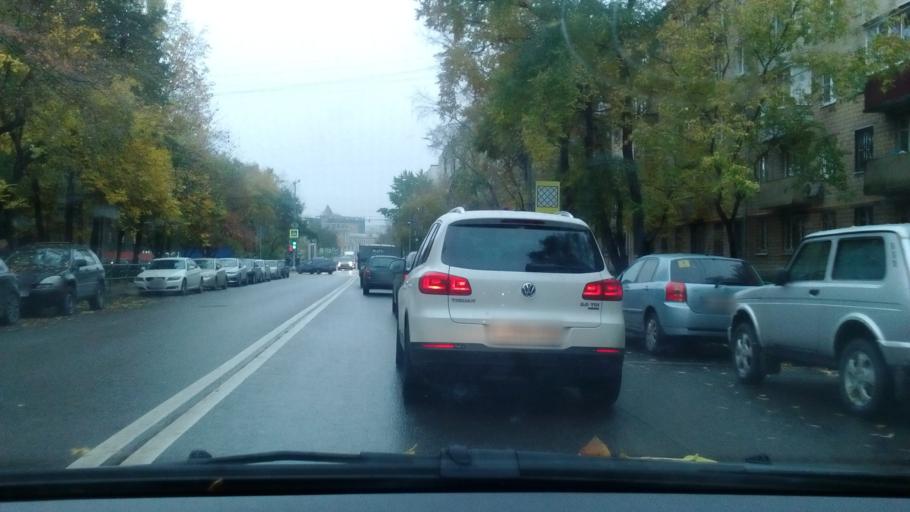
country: RU
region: Moscow
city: Mar'ina Roshcha
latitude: 55.7958
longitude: 37.5765
